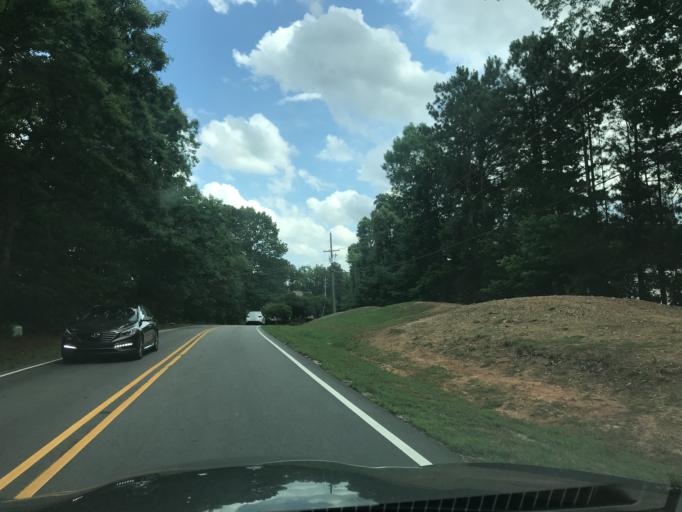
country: US
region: North Carolina
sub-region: Wake County
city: Wake Forest
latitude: 35.9144
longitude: -78.5924
